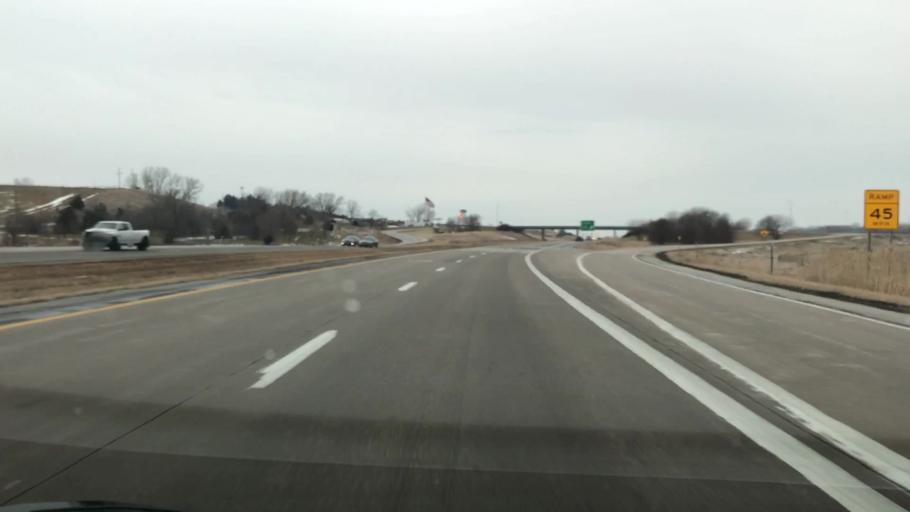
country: US
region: Iowa
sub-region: Pottawattamie County
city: Oakland
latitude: 41.4431
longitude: -95.6075
